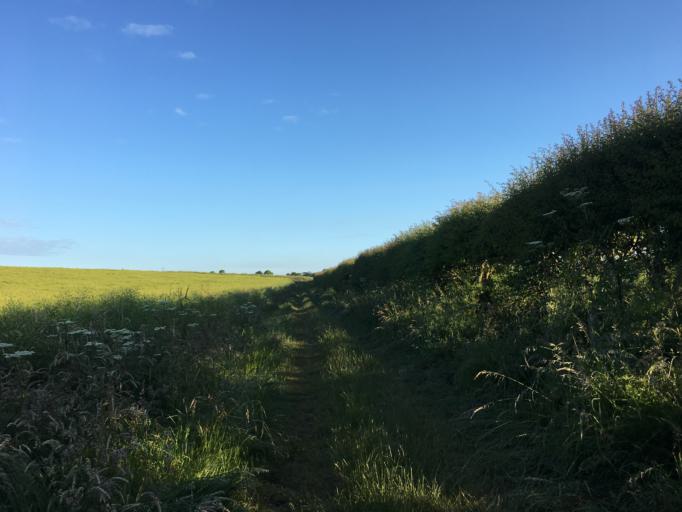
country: GB
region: England
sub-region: Northumberland
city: Bamburgh
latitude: 55.5957
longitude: -1.6946
